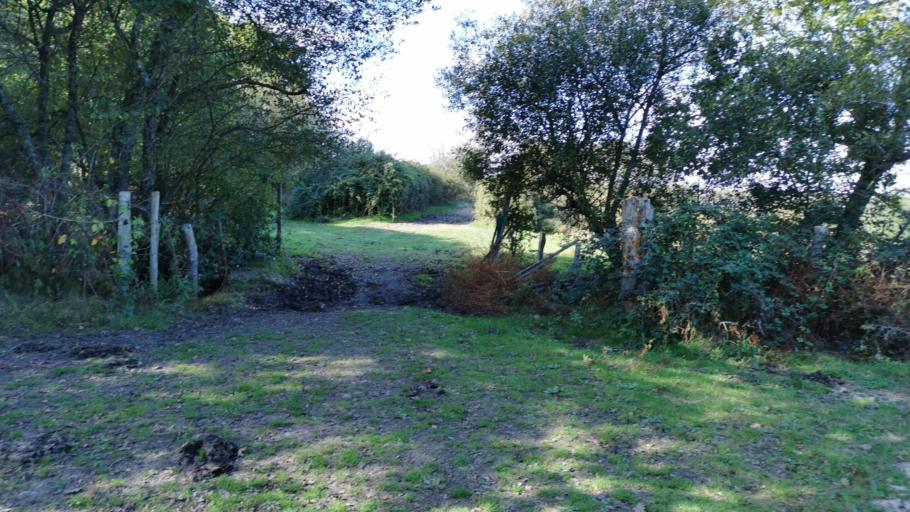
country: FR
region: Pays de la Loire
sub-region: Departement de la Loire-Atlantique
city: Saint-Andre-des-Eaux
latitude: 47.3335
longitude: -2.3050
